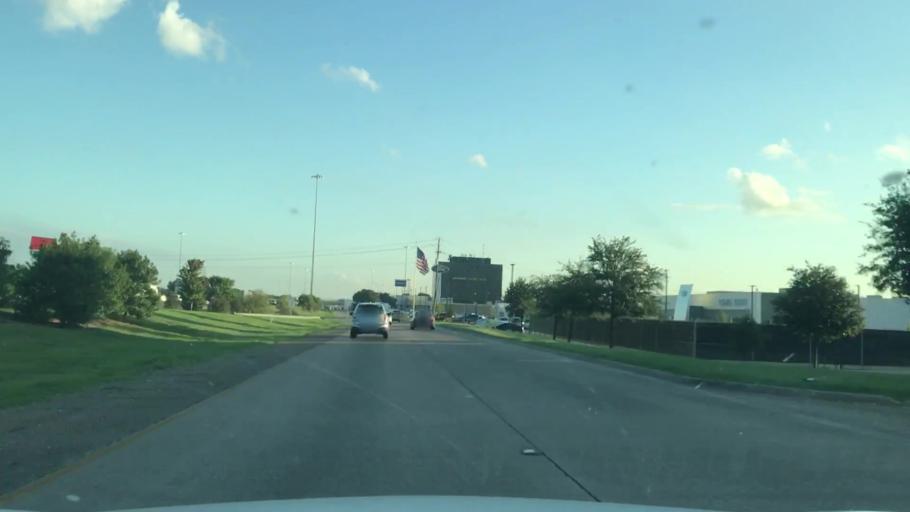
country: US
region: Texas
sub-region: Dallas County
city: Mesquite
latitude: 32.8080
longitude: -96.6280
